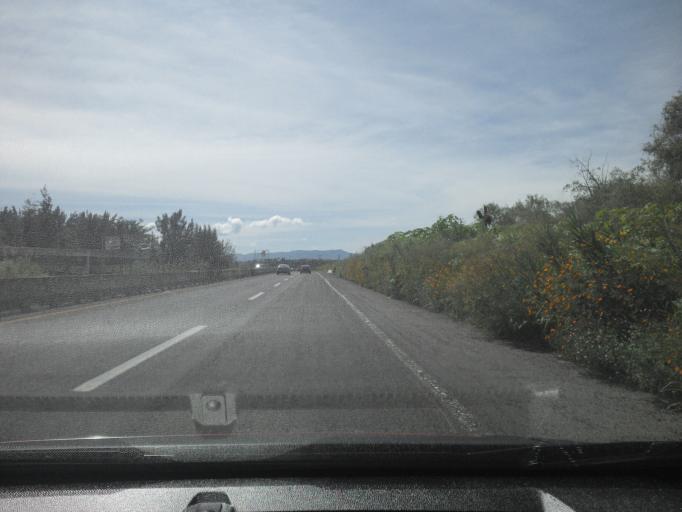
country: MX
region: Jalisco
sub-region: Tala
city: Los Ruisenores
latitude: 20.6881
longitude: -103.6931
